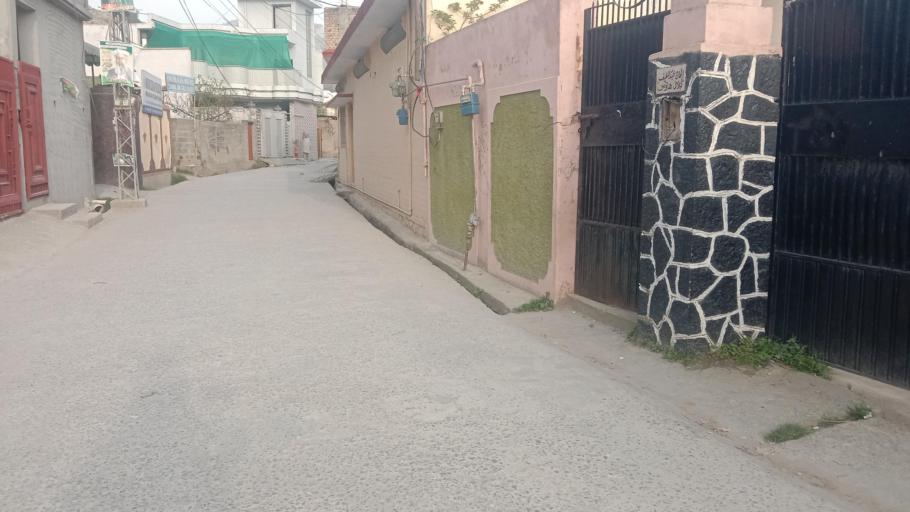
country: PK
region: Khyber Pakhtunkhwa
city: Abbottabad
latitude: 34.1693
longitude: 73.2580
